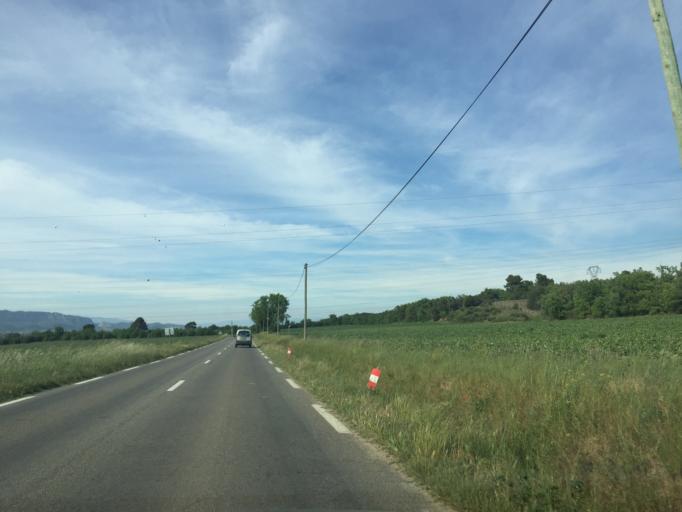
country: FR
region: Provence-Alpes-Cote d'Azur
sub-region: Departement du Var
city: Vinon-sur-Verdon
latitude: 43.7719
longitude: 5.8139
